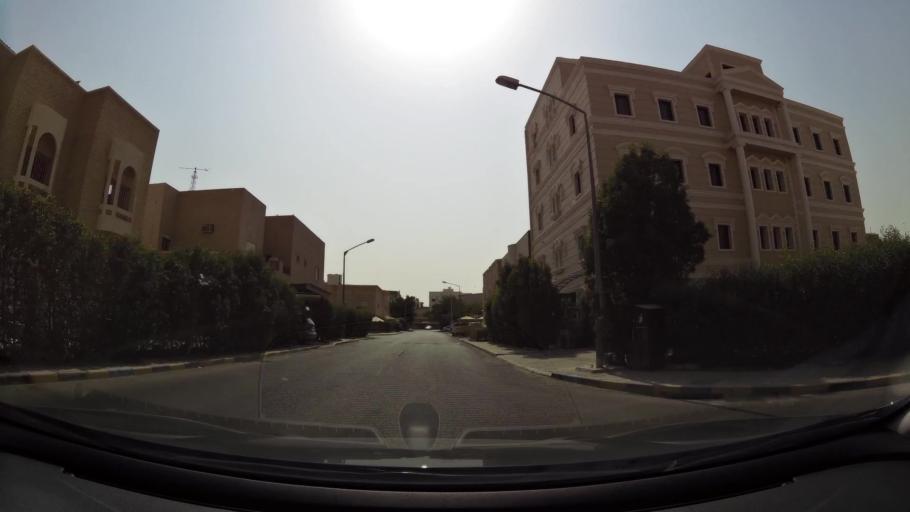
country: KW
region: Muhafazat al Jahra'
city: Al Jahra'
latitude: 29.3193
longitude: 47.6772
